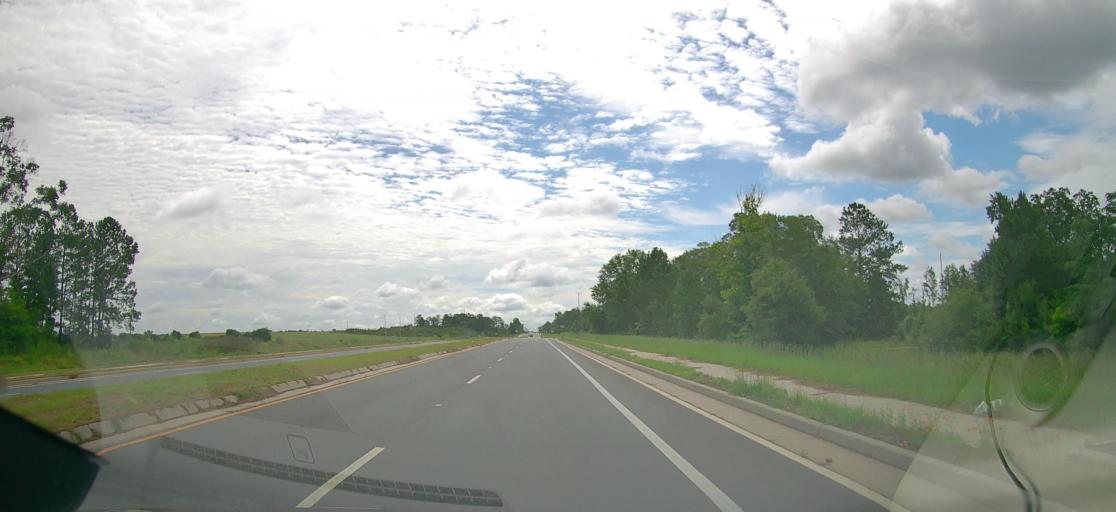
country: US
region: Georgia
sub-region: Houston County
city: Centerville
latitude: 32.6836
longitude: -83.6664
